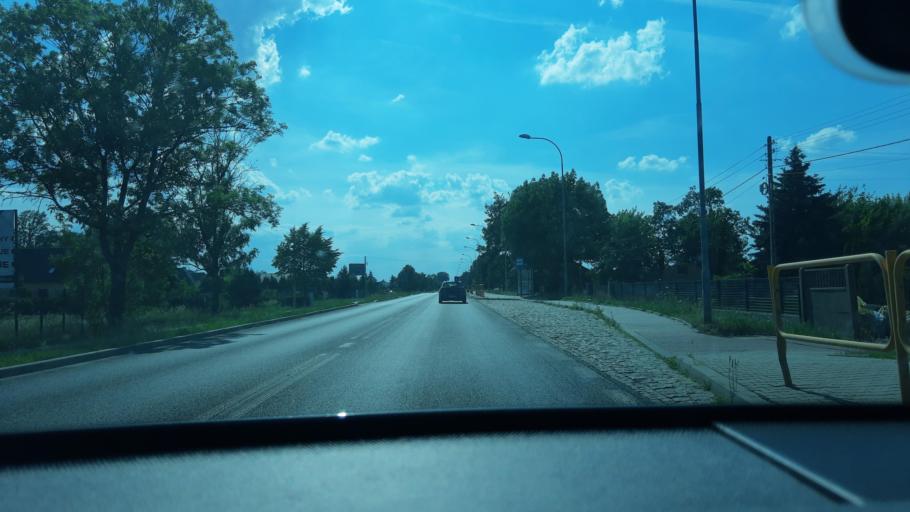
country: PL
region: Lodz Voivodeship
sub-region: Powiat zdunskowolski
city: Zdunska Wola
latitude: 51.6079
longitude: 18.8917
